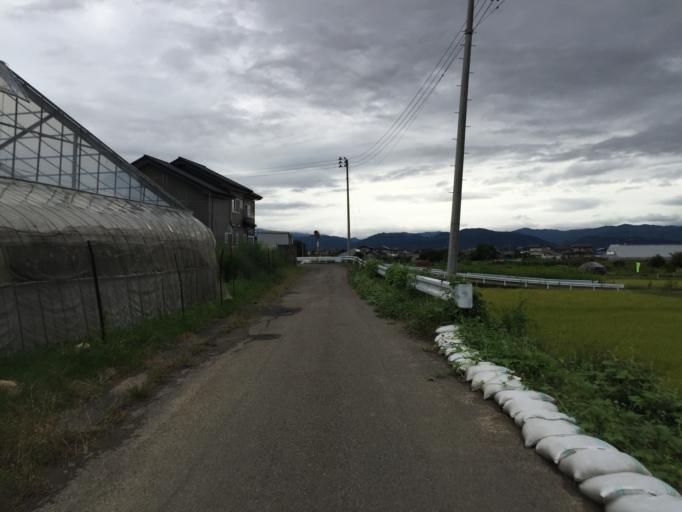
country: JP
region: Fukushima
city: Hobaramachi
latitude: 37.7853
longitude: 140.5108
